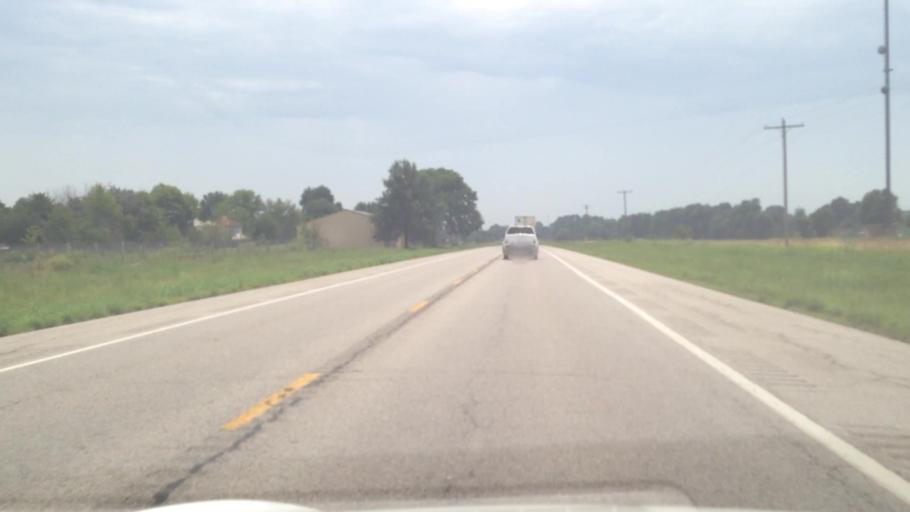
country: US
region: Missouri
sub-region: Jasper County
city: Carl Junction
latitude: 37.2097
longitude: -94.7048
